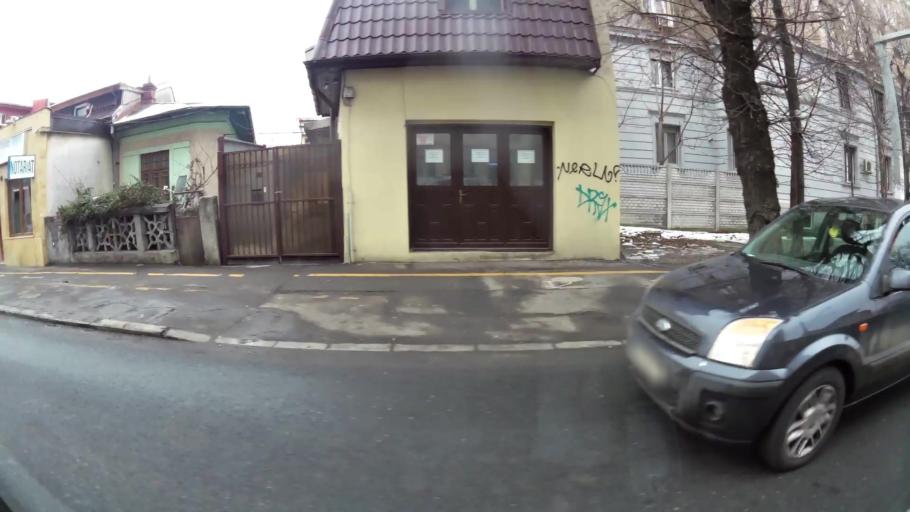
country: RO
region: Bucuresti
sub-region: Municipiul Bucuresti
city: Bucuresti
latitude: 44.4195
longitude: 26.0591
